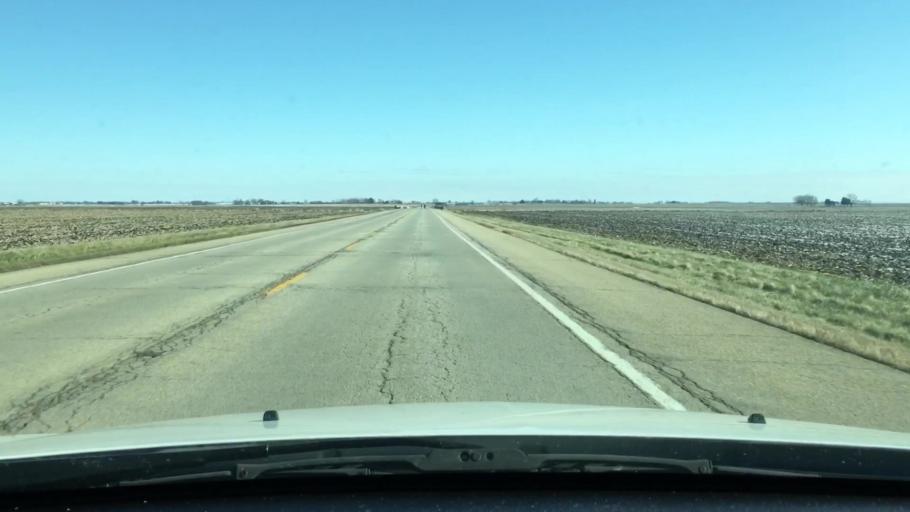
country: US
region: Illinois
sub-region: Ogle County
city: Hillcrest
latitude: 42.0076
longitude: -88.9749
